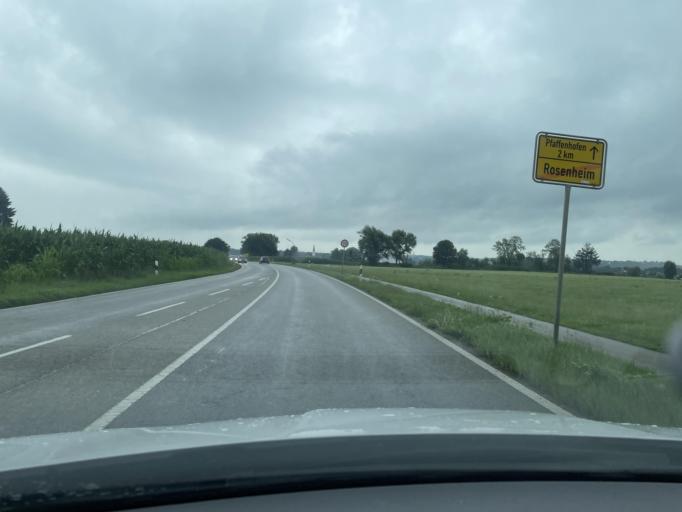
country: DE
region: Bavaria
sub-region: Upper Bavaria
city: Rosenheim
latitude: 47.8796
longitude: 12.1135
